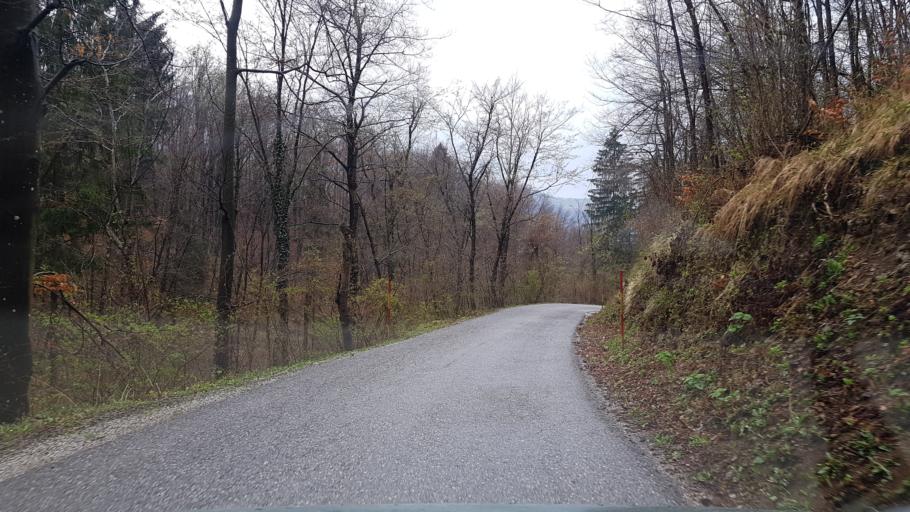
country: SI
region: Tolmin
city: Tolmin
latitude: 46.1422
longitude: 13.8031
